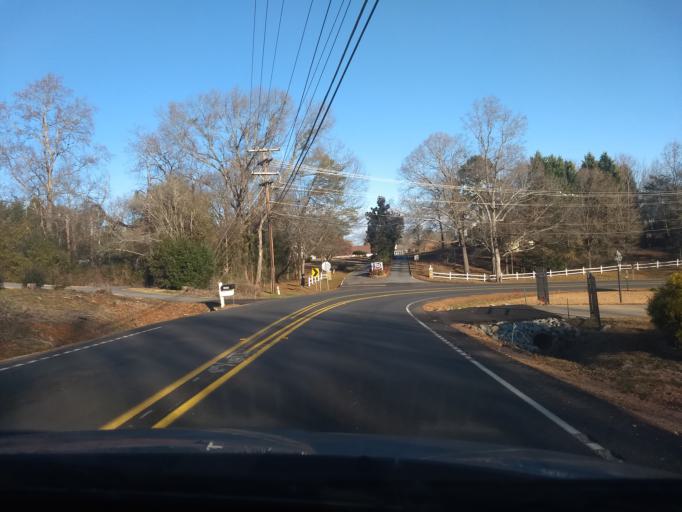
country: US
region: South Carolina
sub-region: Greenville County
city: Greer
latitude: 34.9735
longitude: -82.2002
